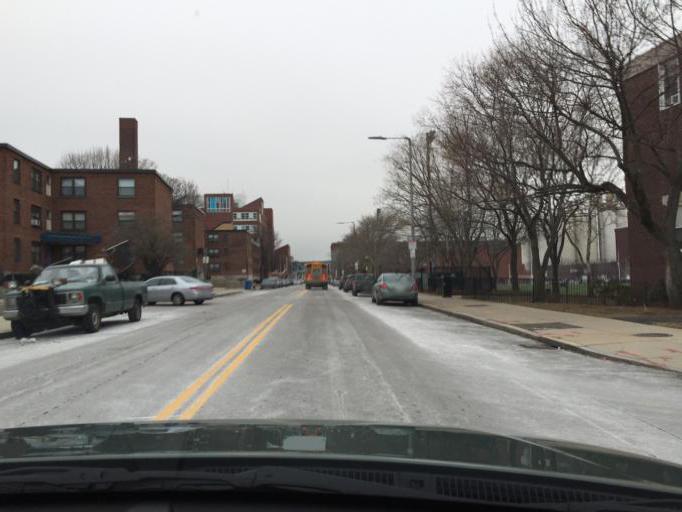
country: US
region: Massachusetts
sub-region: Suffolk County
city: Boston
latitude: 42.3796
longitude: -71.0586
